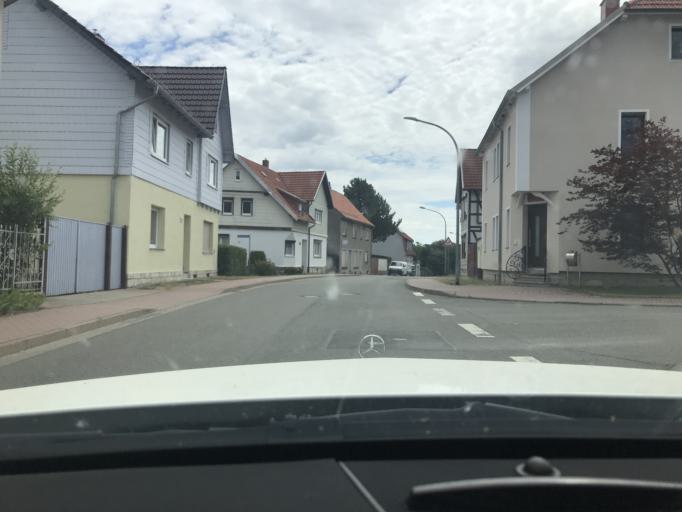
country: DE
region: Thuringia
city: Menteroda
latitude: 51.3076
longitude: 10.5643
